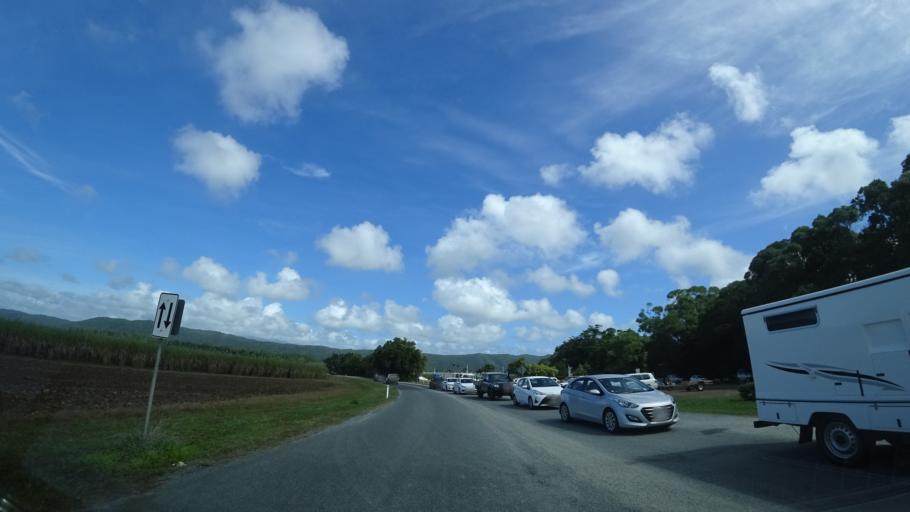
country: AU
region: Queensland
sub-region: Cairns
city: Port Douglas
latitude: -16.2618
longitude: 145.3943
